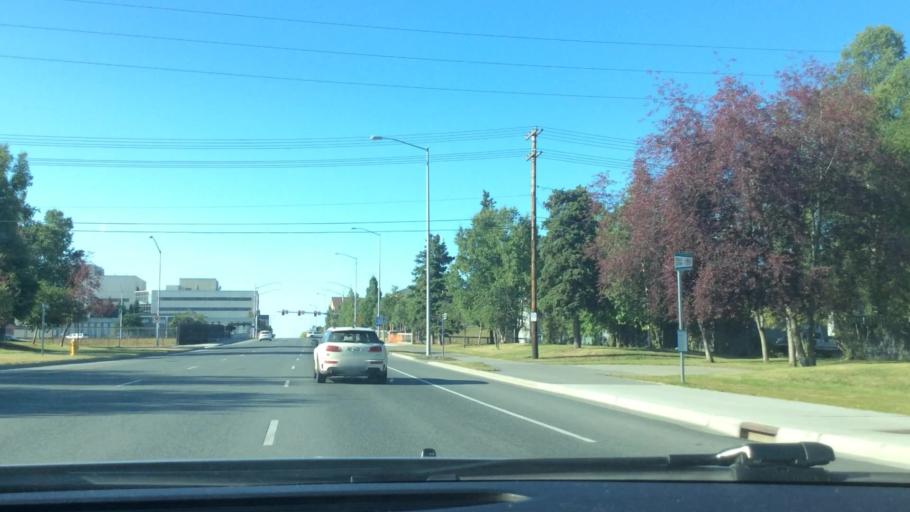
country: US
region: Alaska
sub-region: Anchorage Municipality
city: Anchorage
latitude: 61.2118
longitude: -149.8829
